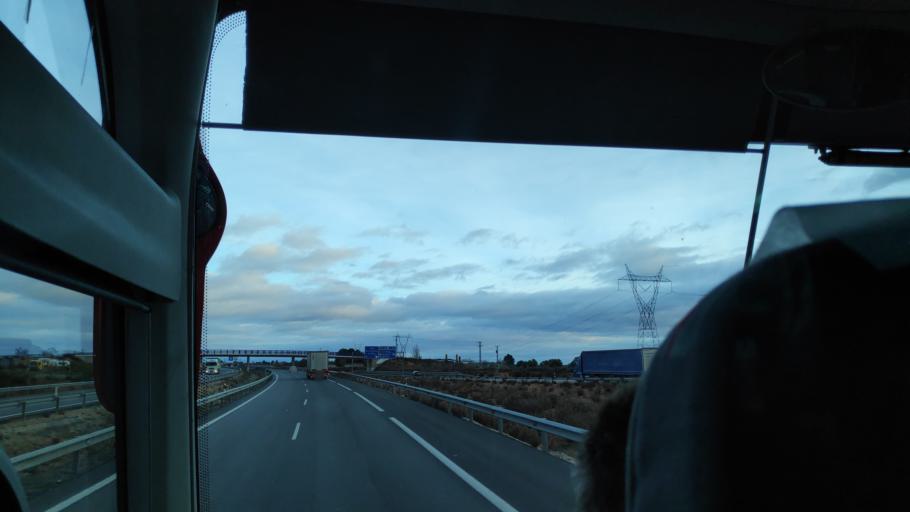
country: ES
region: Castille-La Mancha
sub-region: Provincia de Cuenca
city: Tarancon
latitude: 39.9986
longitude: -3.0203
